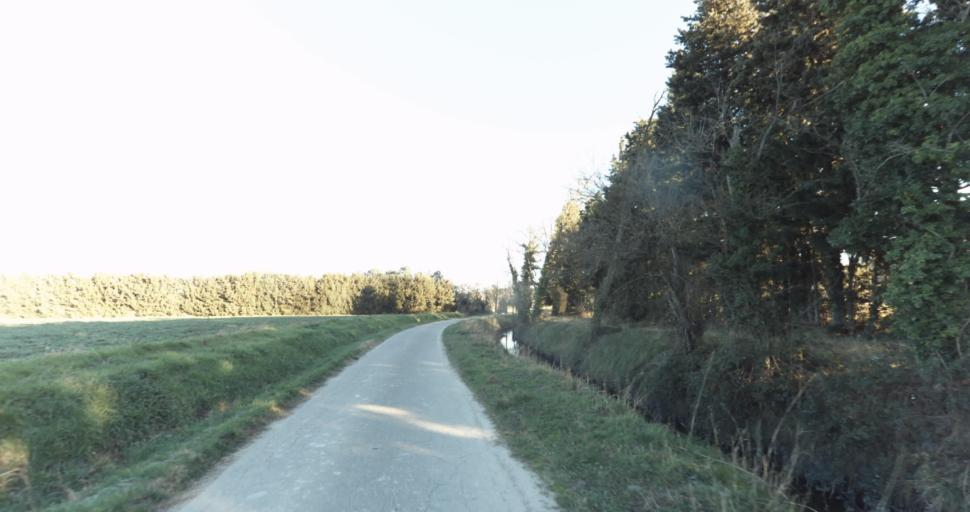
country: FR
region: Provence-Alpes-Cote d'Azur
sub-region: Departement des Bouches-du-Rhone
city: Barbentane
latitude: 43.9033
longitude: 4.7293
